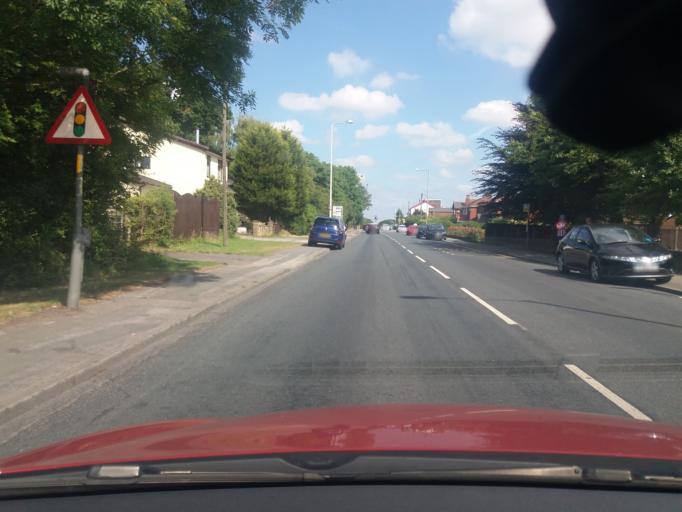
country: GB
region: England
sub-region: Lancashire
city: Chorley
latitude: 53.6318
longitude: -2.6123
